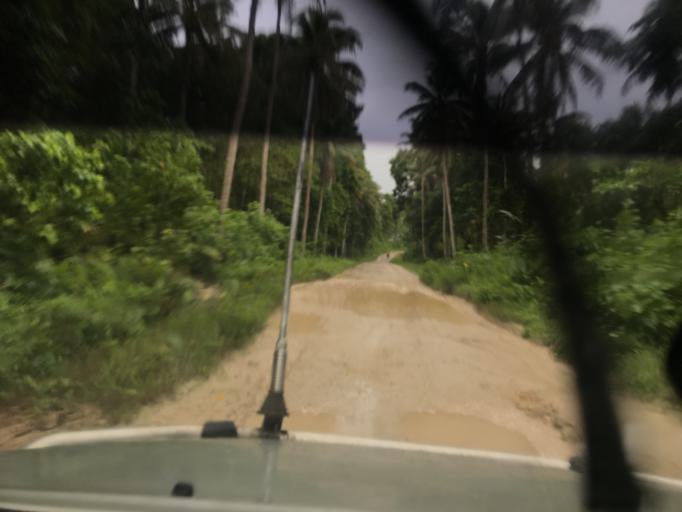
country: SB
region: Malaita
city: Auki
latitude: -9.0313
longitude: 160.7987
